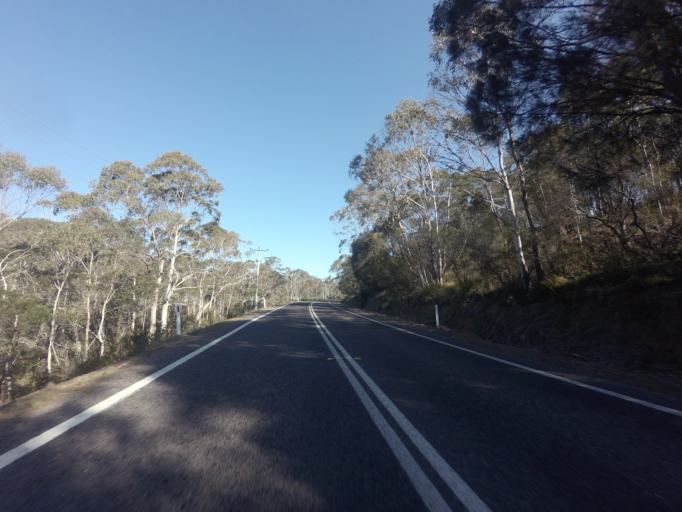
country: AU
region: Tasmania
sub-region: Sorell
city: Sorell
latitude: -42.4053
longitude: 147.9345
